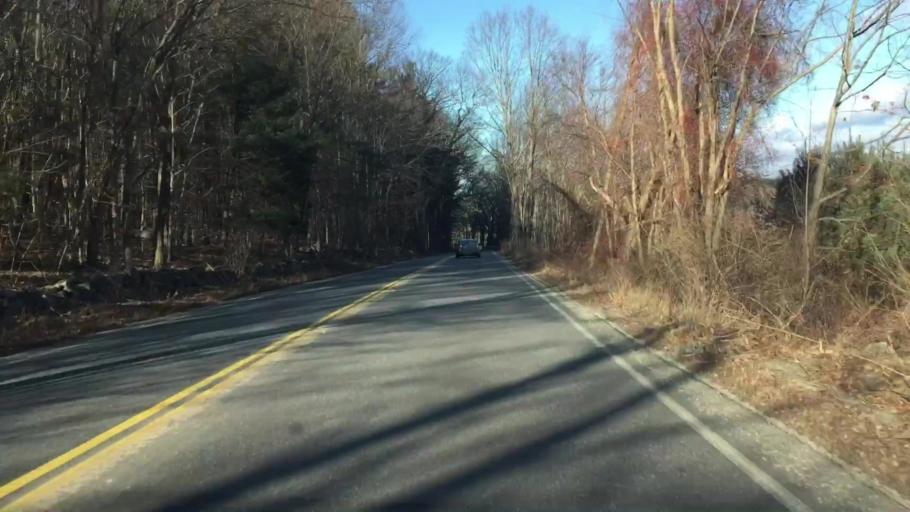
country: US
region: Massachusetts
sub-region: Worcester County
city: Sterling
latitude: 42.4244
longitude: -71.8087
